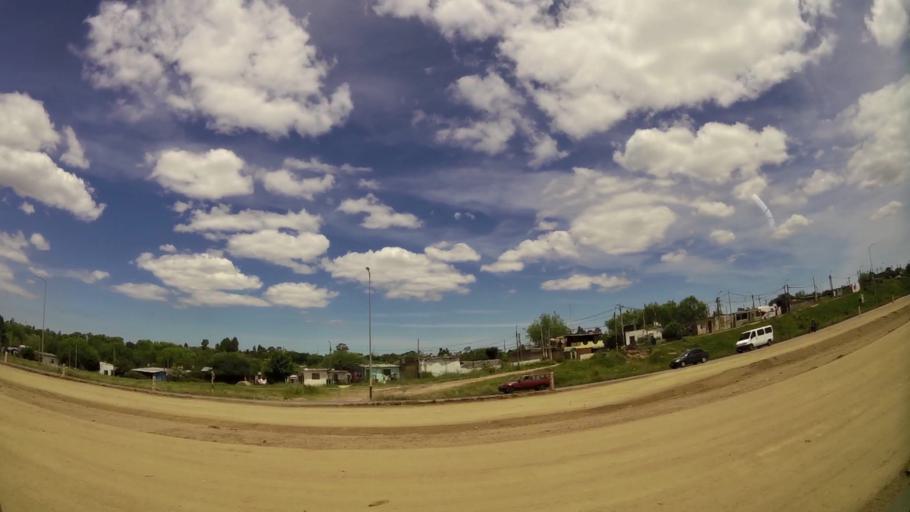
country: UY
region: Montevideo
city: Pajas Blancas
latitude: -34.8527
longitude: -56.2665
